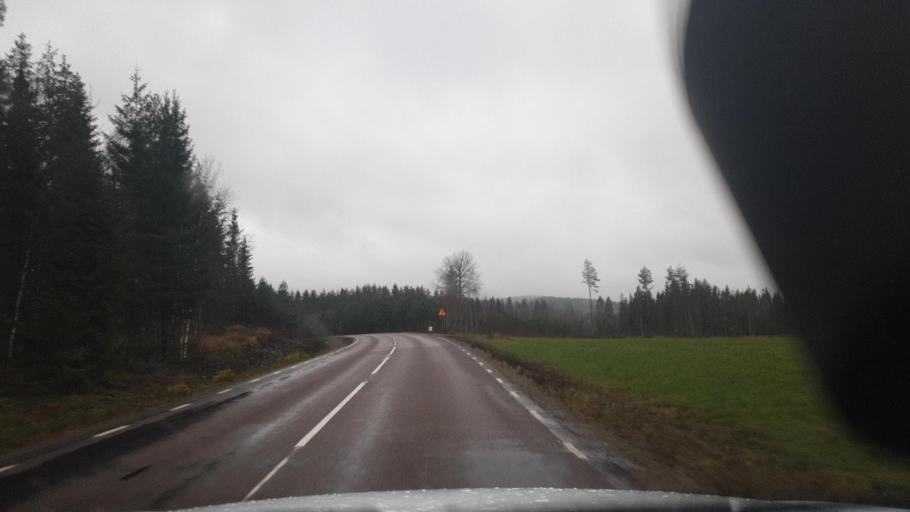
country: SE
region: Vaermland
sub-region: Eda Kommun
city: Amotfors
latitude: 59.7330
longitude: 12.1702
